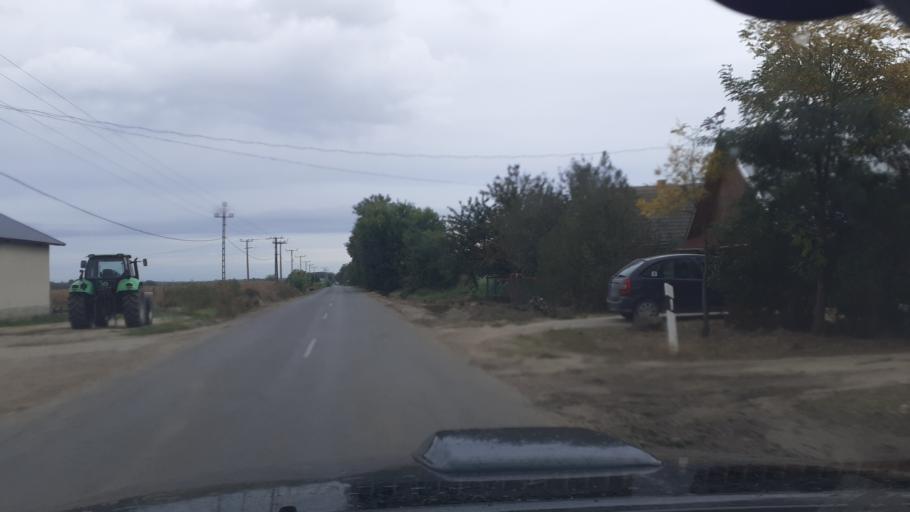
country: HU
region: Tolna
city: Dunafoldvar
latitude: 46.7841
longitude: 18.9420
